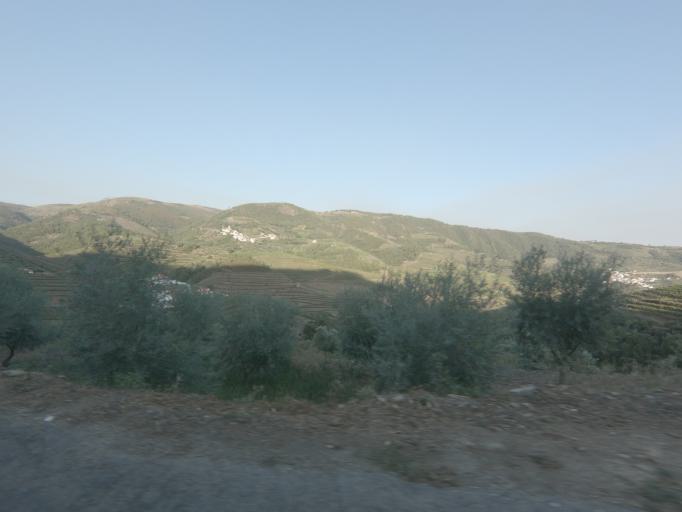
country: PT
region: Vila Real
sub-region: Sabrosa
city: Vilela
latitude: 41.2014
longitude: -7.6490
